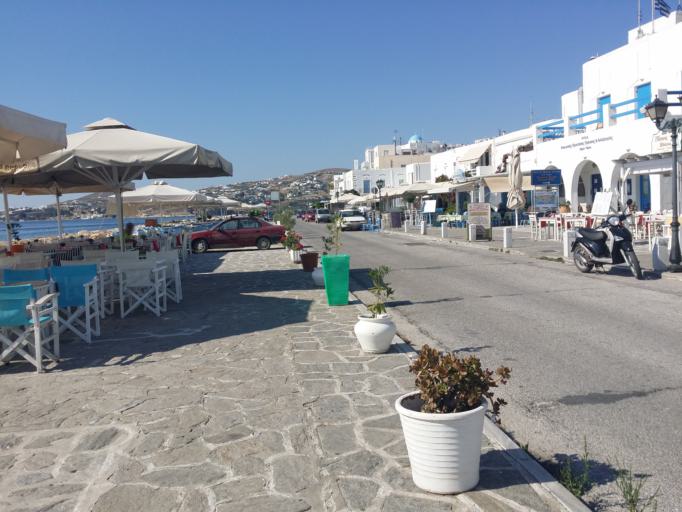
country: GR
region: South Aegean
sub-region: Nomos Kykladon
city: Paros
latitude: 37.0829
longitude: 25.1462
